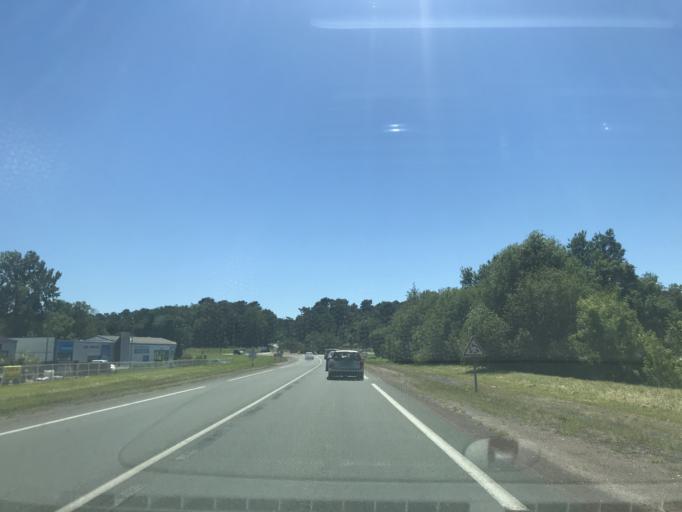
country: FR
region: Poitou-Charentes
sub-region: Departement de la Charente-Maritime
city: Saint-Georges-de-Didonne
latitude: 45.5983
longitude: -0.9745
